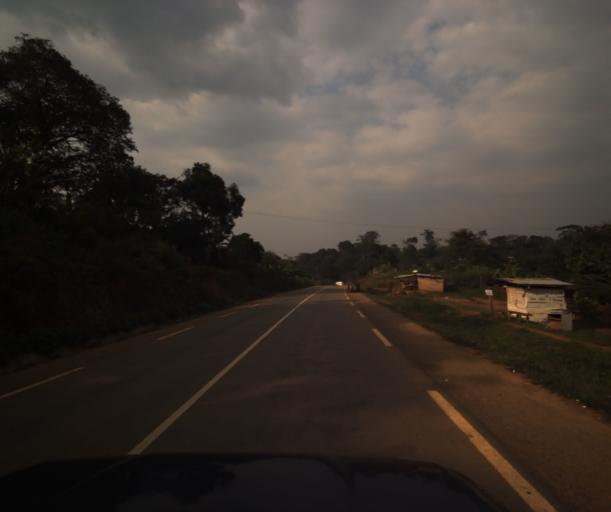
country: CM
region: Centre
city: Mbankomo
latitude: 3.7664
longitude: 11.4061
